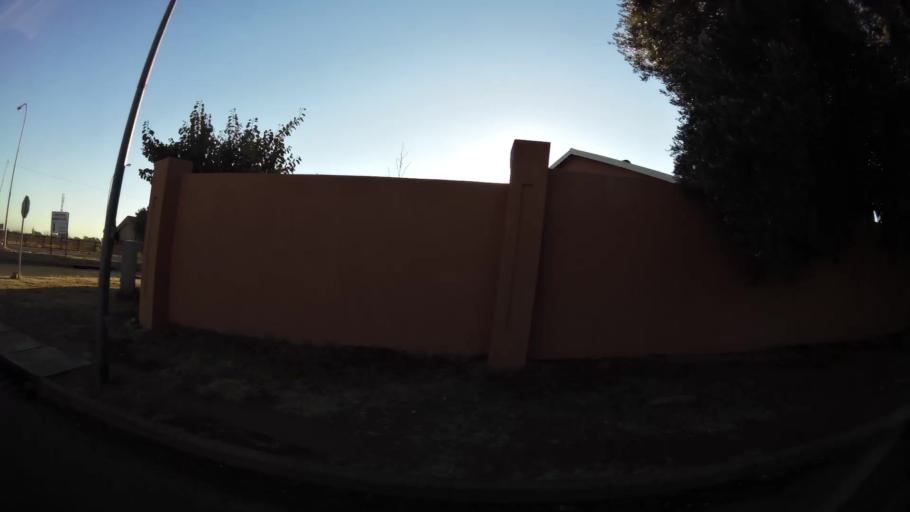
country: ZA
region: Northern Cape
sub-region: Frances Baard District Municipality
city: Kimberley
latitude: -28.7521
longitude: 24.7353
